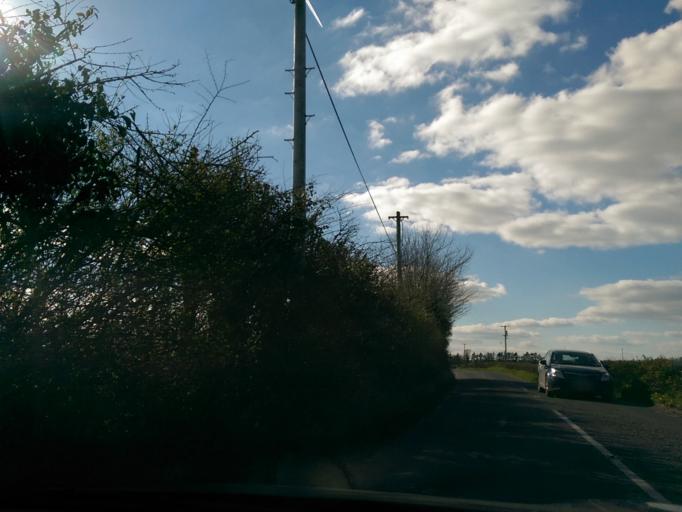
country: IE
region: Leinster
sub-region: Uibh Fhaili
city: Banagher
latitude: 53.1081
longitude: -8.0704
